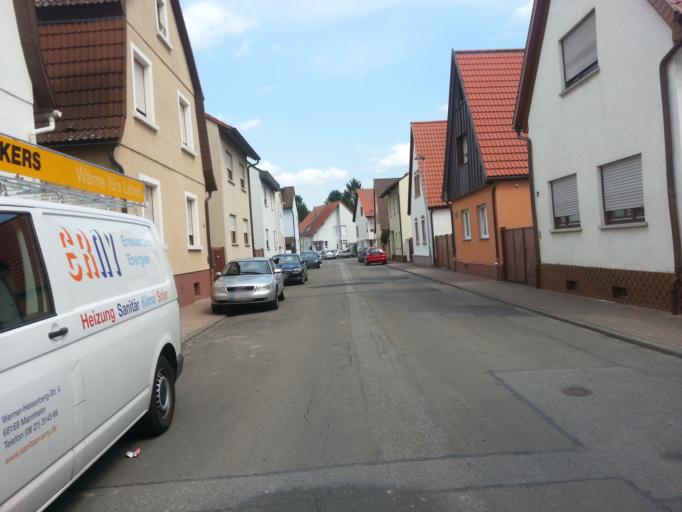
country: DE
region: Baden-Wuerttemberg
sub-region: Karlsruhe Region
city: Heddesheim
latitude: 49.5073
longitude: 8.6007
